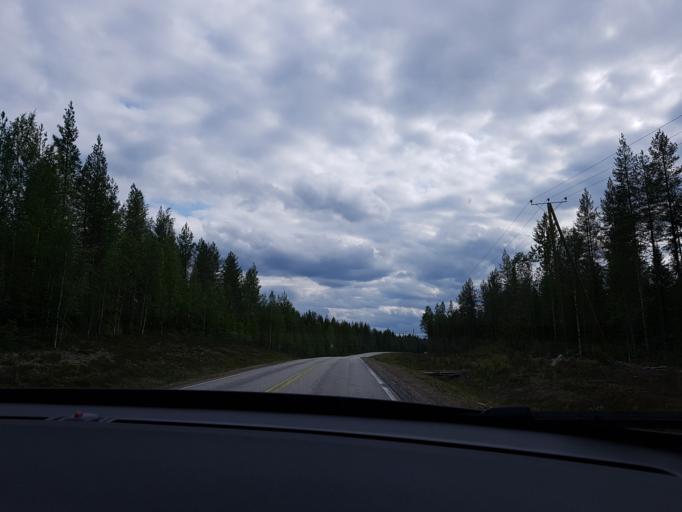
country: FI
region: Kainuu
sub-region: Kehys-Kainuu
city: Kuhmo
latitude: 64.2996
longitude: 29.8529
